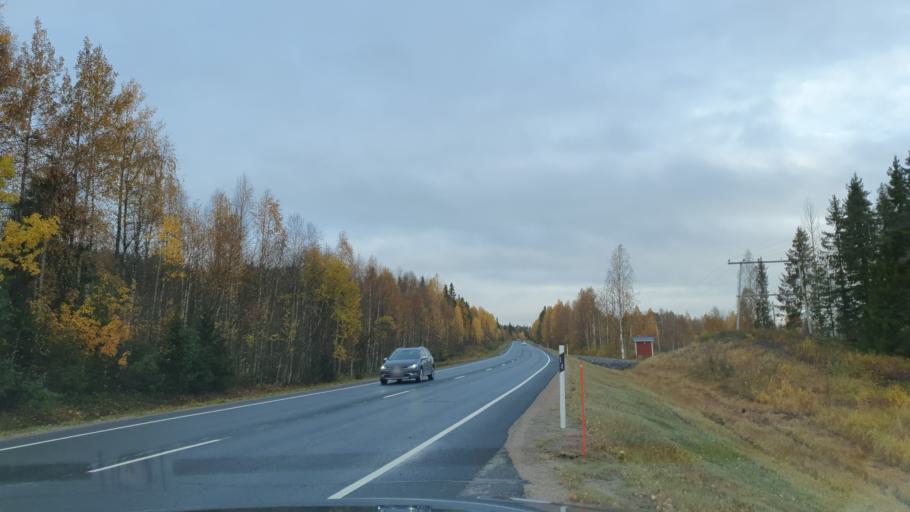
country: FI
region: Lapland
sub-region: Rovaniemi
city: Rovaniemi
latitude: 66.6108
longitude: 25.5655
